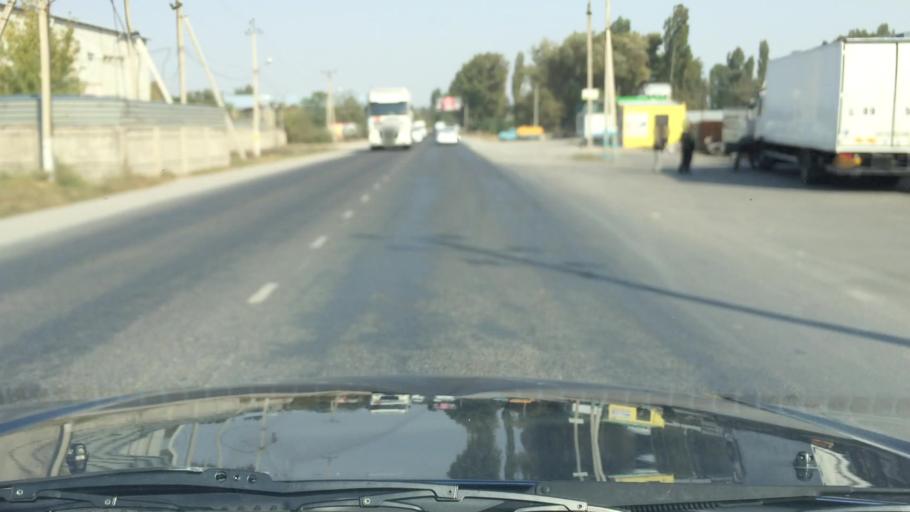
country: KG
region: Chuy
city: Lebedinovka
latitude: 42.8900
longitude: 74.6797
